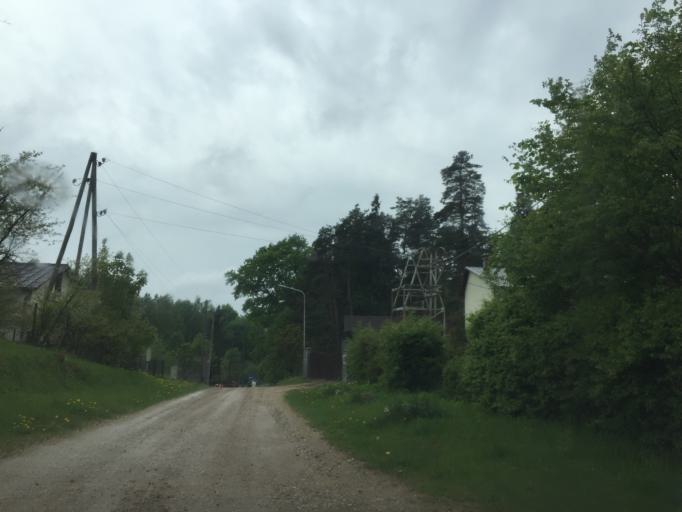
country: LV
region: Kegums
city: Kegums
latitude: 56.7477
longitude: 24.7316
